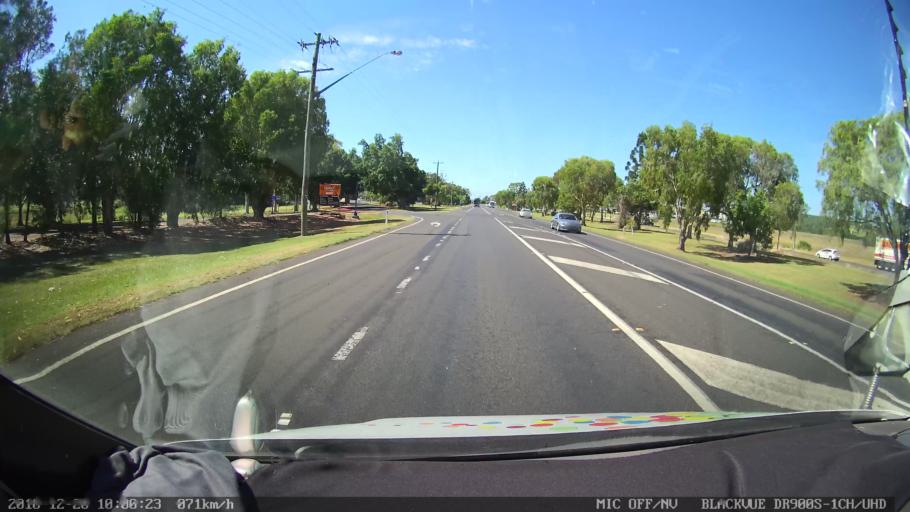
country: AU
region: New South Wales
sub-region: Lismore Municipality
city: Lismore
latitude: -28.8320
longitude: 153.2648
